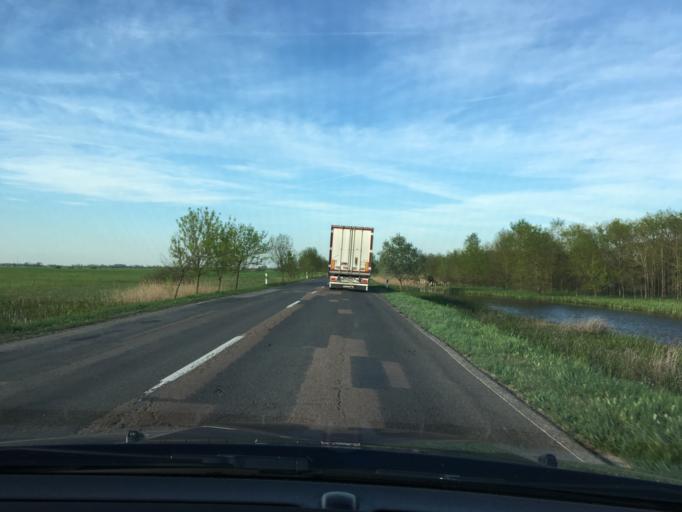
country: HU
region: Hajdu-Bihar
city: Berettyoujfalu
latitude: 47.1629
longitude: 21.5083
